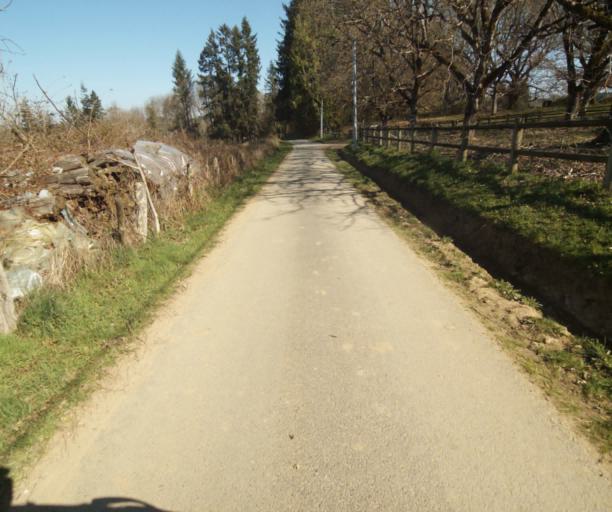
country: FR
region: Limousin
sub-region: Departement de la Correze
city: Saint-Mexant
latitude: 45.2952
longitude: 1.6072
